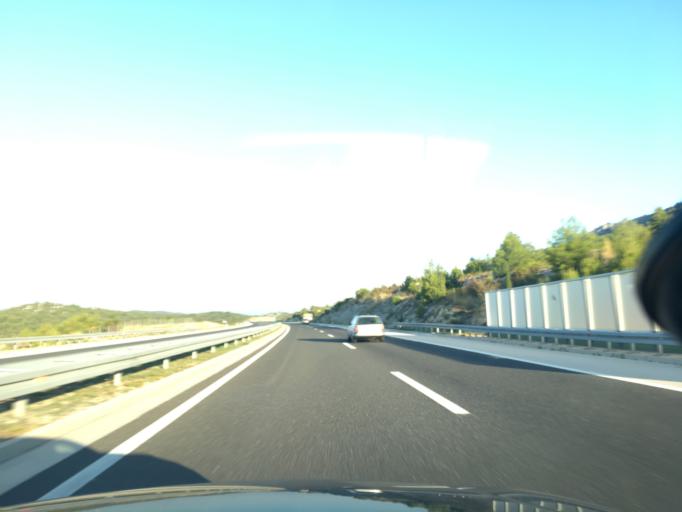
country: HR
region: Sibensko-Kniniska
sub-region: Grad Sibenik
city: Sibenik
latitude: 43.7503
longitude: 15.9526
